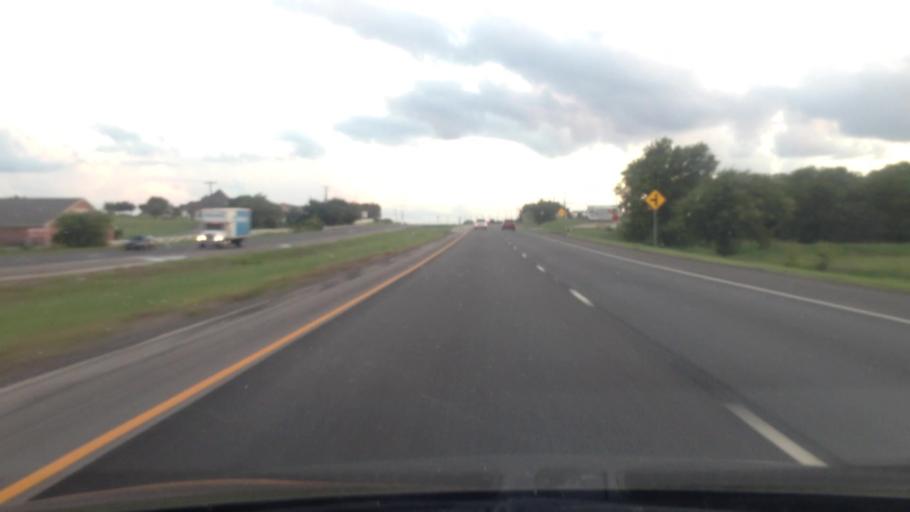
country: US
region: Texas
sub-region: Parker County
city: Aledo
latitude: 32.5799
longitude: -97.5992
